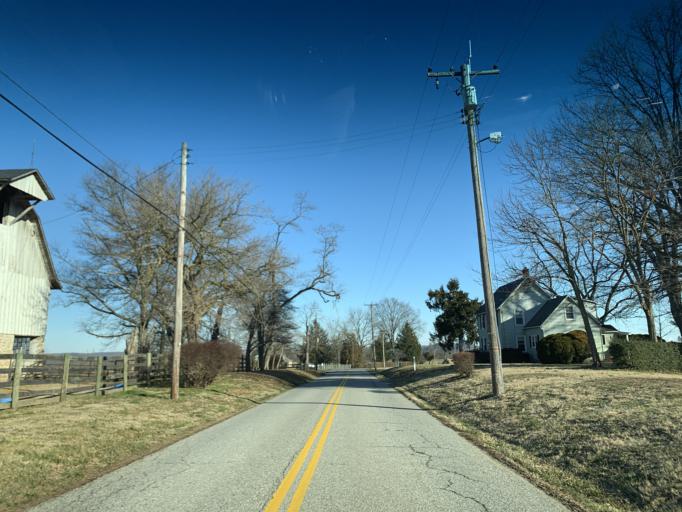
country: US
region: Maryland
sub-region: Harford County
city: Aberdeen
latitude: 39.5785
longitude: -76.2351
